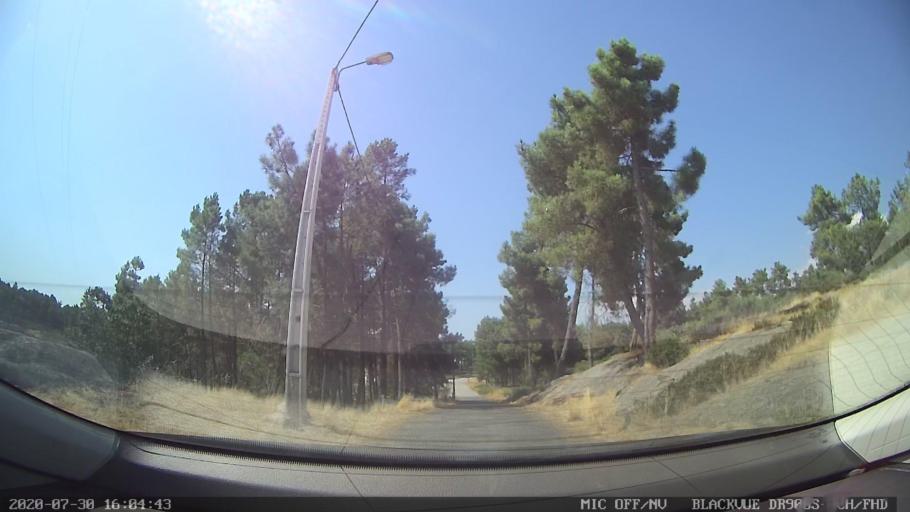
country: PT
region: Vila Real
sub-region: Murca
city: Murca
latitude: 41.3498
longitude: -7.4855
